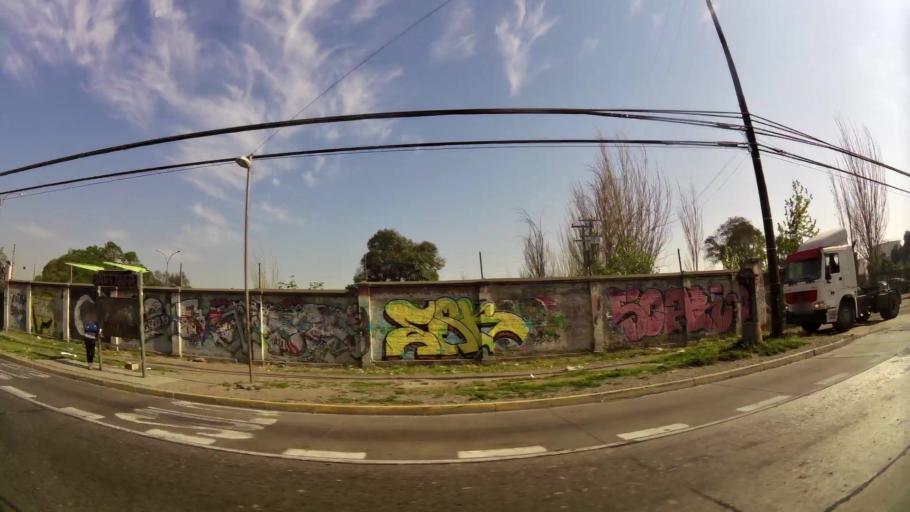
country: CL
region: Santiago Metropolitan
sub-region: Provincia de Santiago
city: Lo Prado
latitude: -33.5224
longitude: -70.7477
